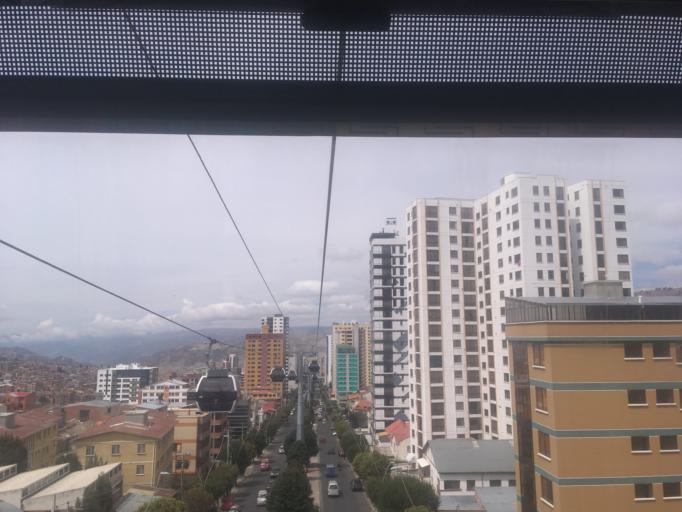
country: BO
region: La Paz
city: La Paz
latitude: -16.4853
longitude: -68.1218
